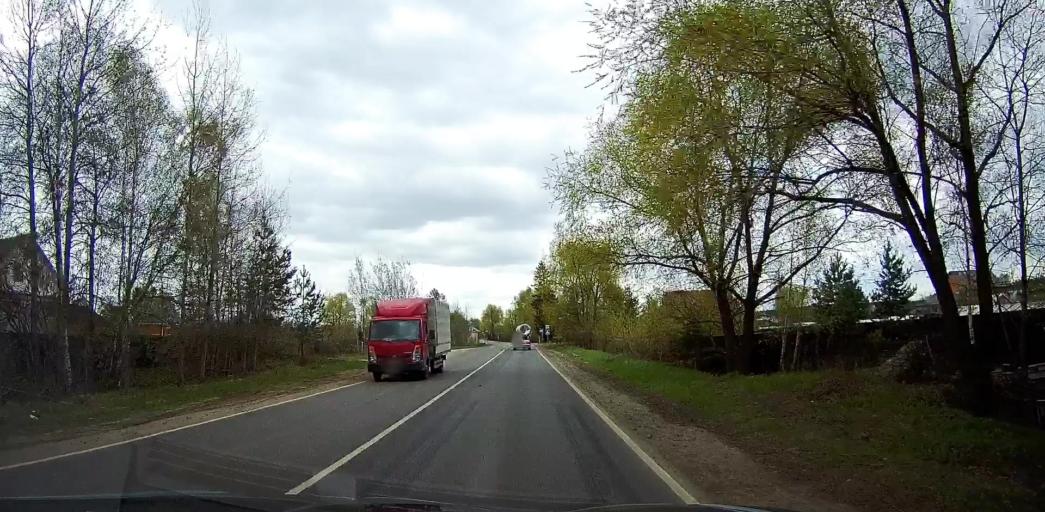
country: RU
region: Moskovskaya
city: Beloozerskiy
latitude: 55.5171
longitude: 38.4333
